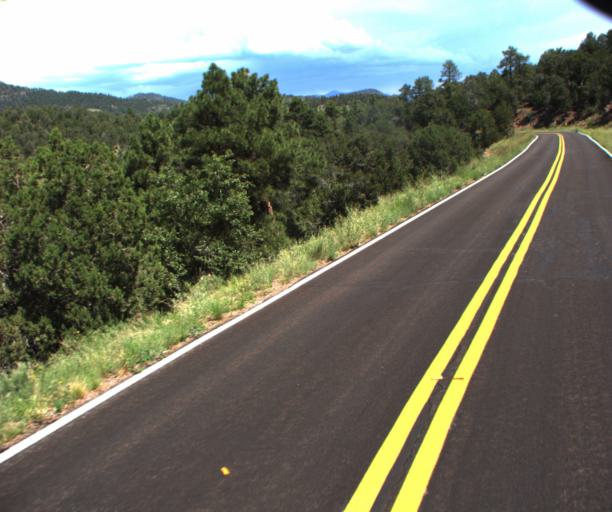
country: US
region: Arizona
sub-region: Greenlee County
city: Morenci
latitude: 33.4034
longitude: -109.3490
